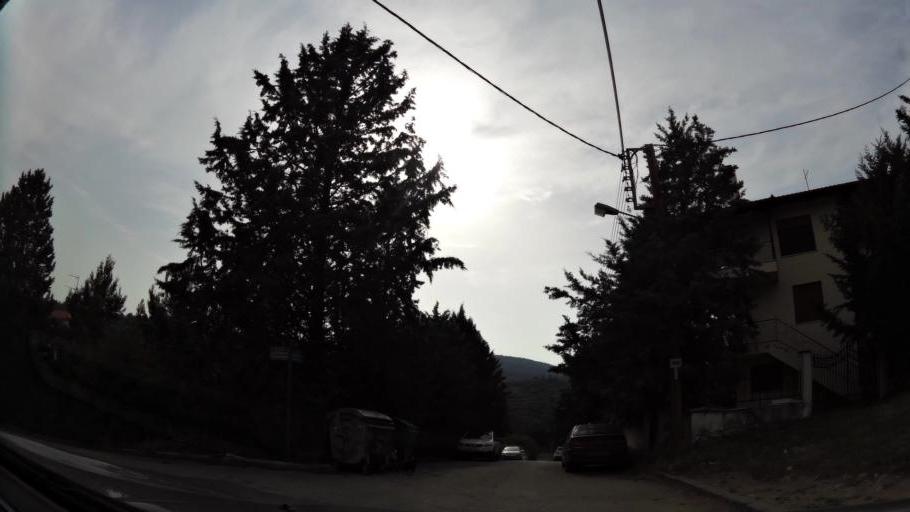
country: GR
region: Central Macedonia
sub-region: Nomos Thessalonikis
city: Oraiokastro
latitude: 40.7330
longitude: 22.9116
